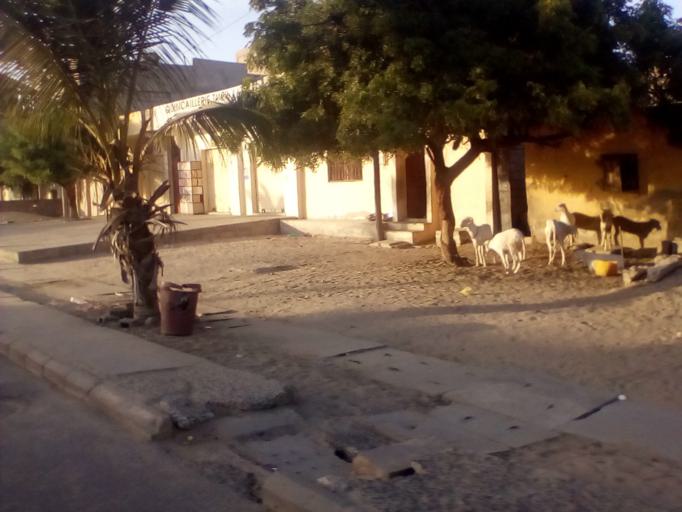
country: SN
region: Saint-Louis
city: Saint-Louis
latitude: 16.0194
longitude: -16.4954
